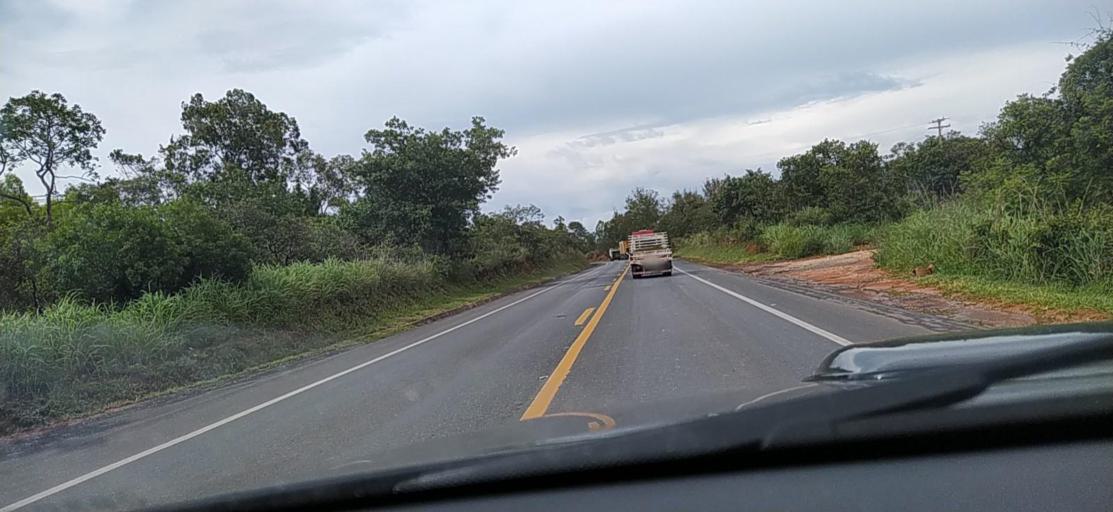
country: BR
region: Minas Gerais
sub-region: Montes Claros
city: Montes Claros
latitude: -16.8407
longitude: -43.8496
